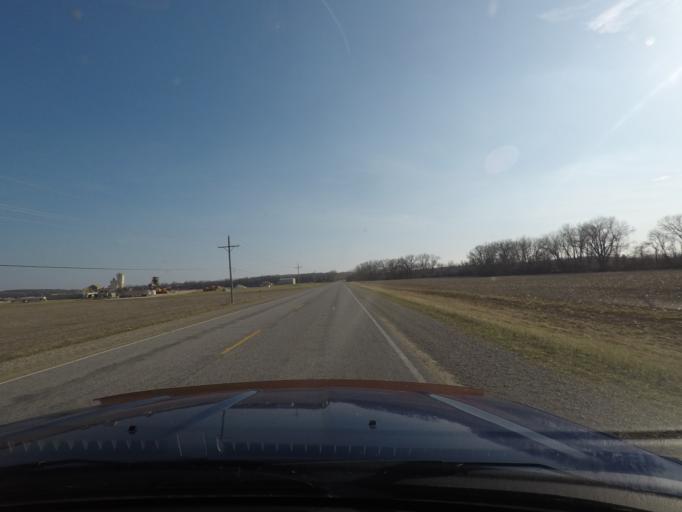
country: US
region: Kansas
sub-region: Jefferson County
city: Oskaloosa
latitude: 39.0600
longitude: -95.3825
